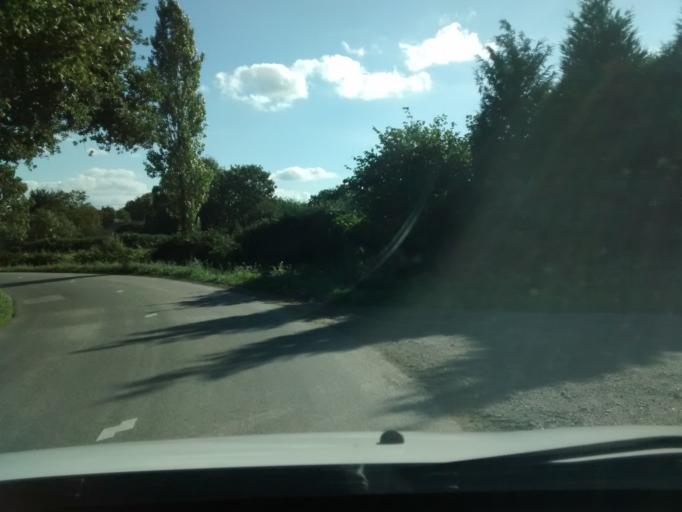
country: FR
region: Brittany
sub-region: Departement d'Ille-et-Vilaine
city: Chantepie
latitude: 48.0930
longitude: -1.5850
